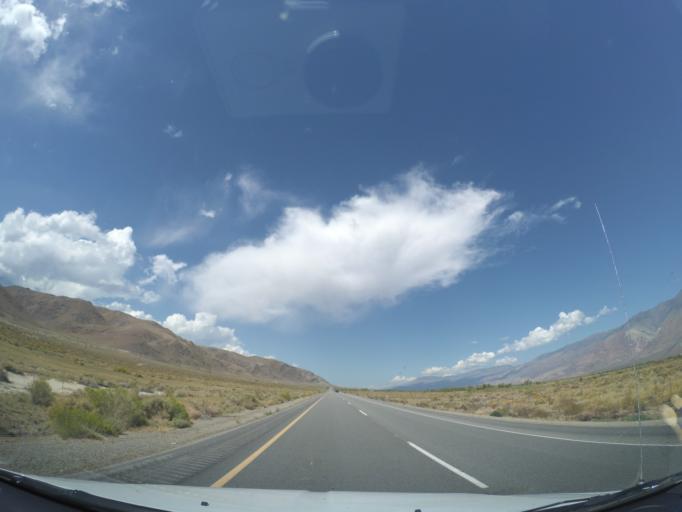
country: US
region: California
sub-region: Inyo County
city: Lone Pine
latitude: 36.6451
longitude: -118.0820
